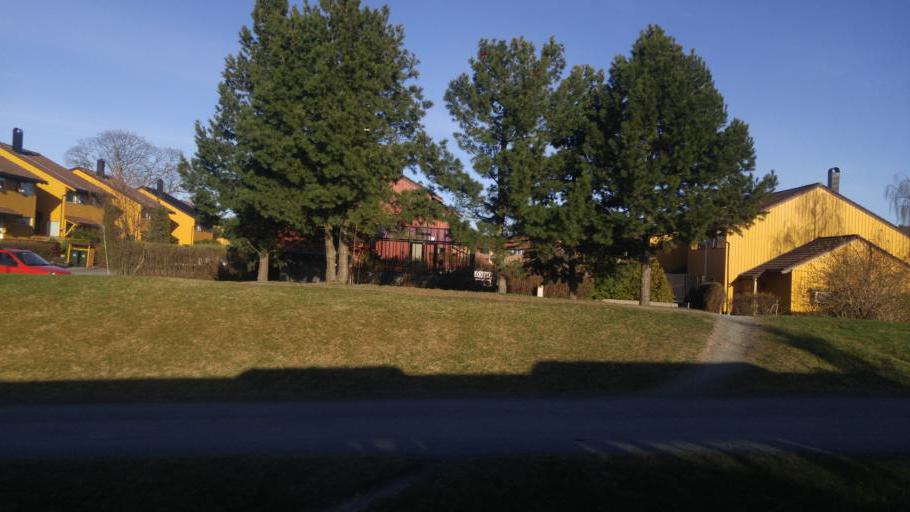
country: NO
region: Sor-Trondelag
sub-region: Trondheim
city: Trondheim
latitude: 63.4169
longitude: 10.4469
